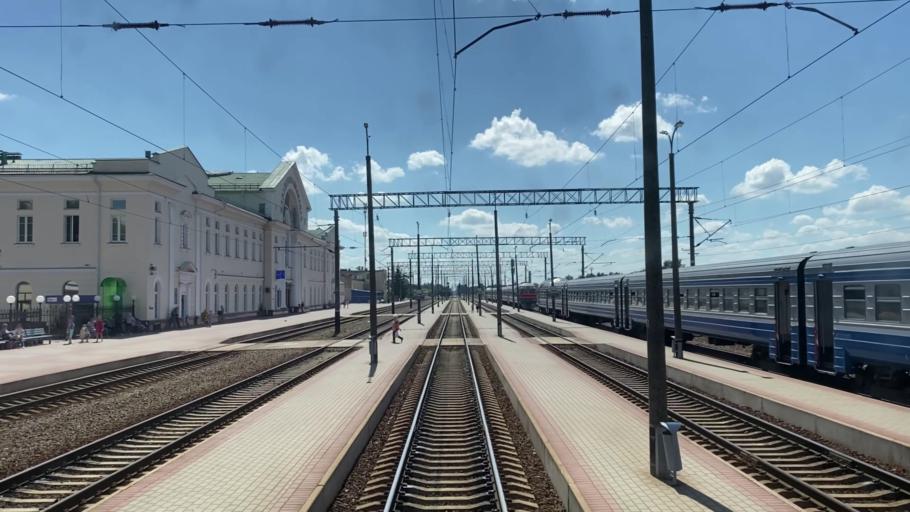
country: BY
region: Brest
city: Baranovichi
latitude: 53.1300
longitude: 26.0414
